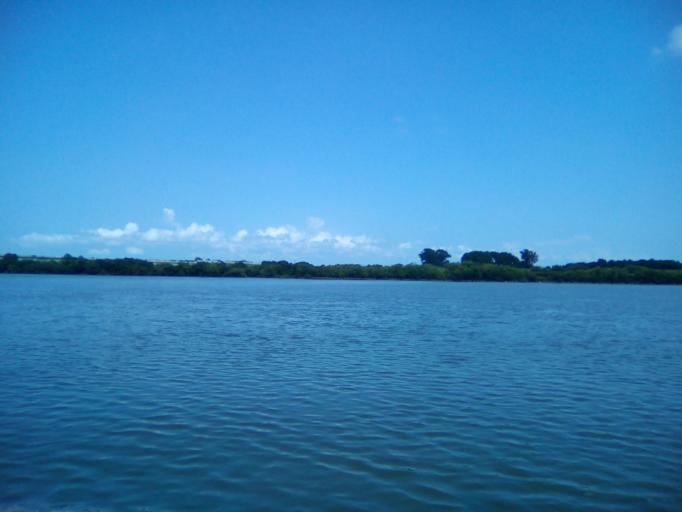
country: JP
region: Hokkaido
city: Ebetsu
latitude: 43.1331
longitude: 141.5161
